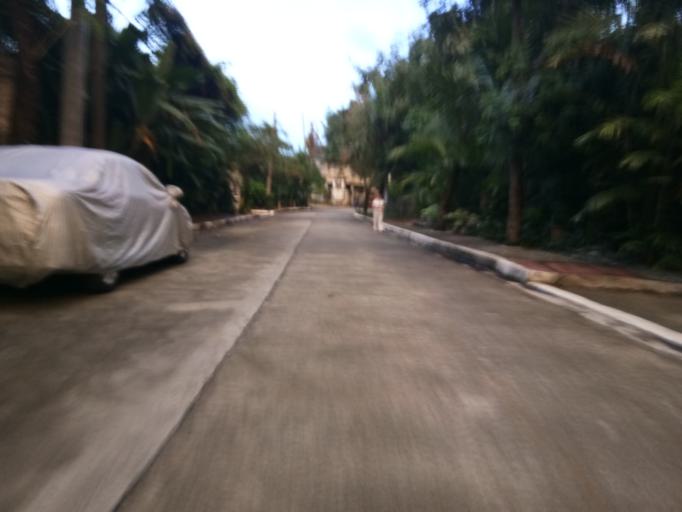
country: PH
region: Metro Manila
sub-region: San Juan
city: San Juan
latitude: 14.6141
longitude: 121.0441
